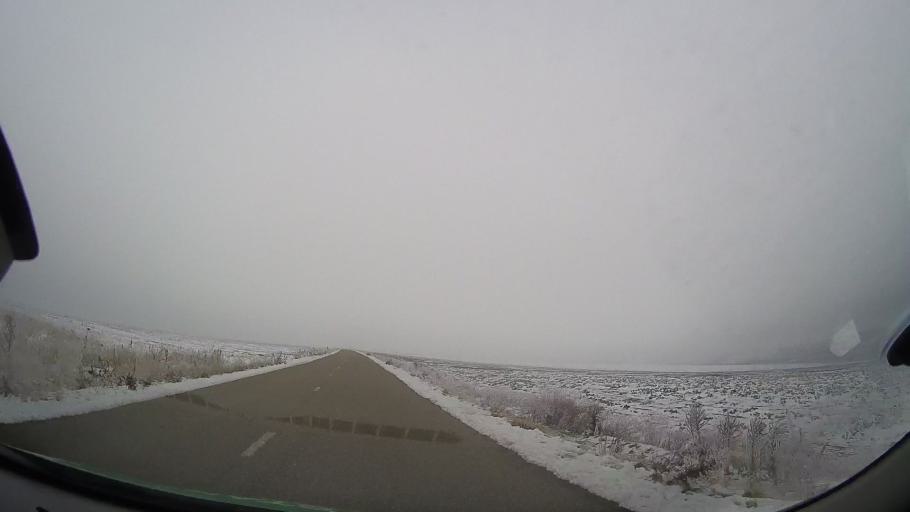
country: RO
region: Vaslui
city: Coroiesti
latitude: 46.2163
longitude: 27.4805
